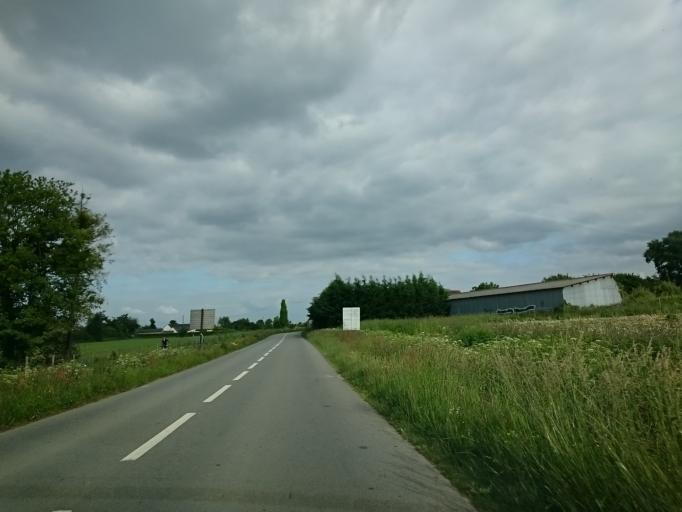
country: FR
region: Brittany
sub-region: Departement d'Ille-et-Vilaine
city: Laille
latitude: 47.9775
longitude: -1.7081
